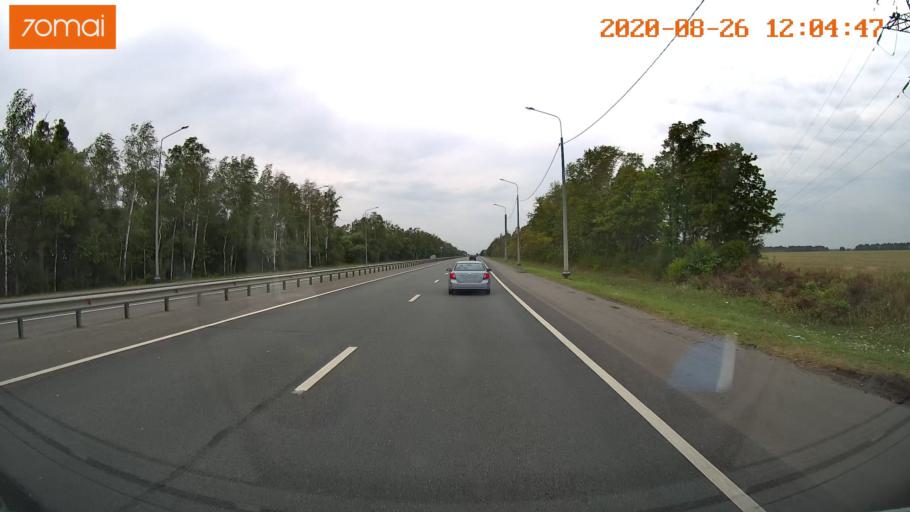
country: RU
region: Rjazan
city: Kiritsy
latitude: 54.3142
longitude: 40.1806
